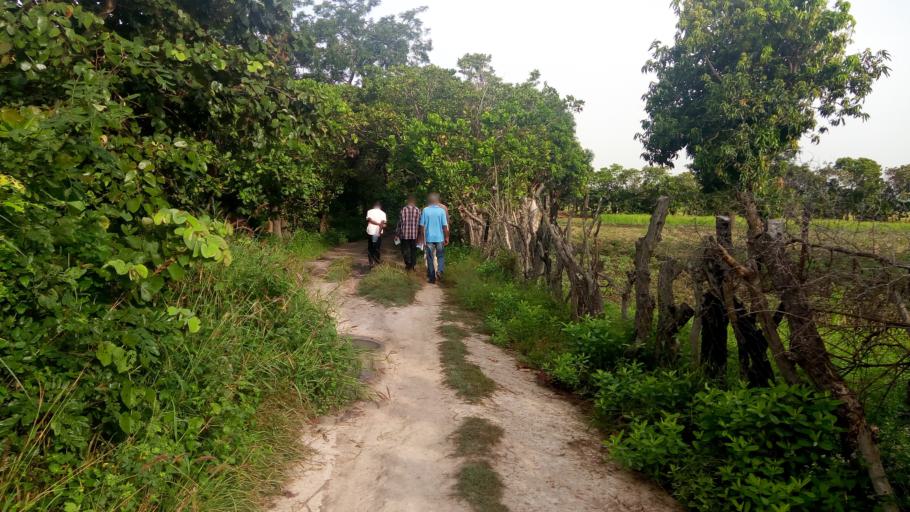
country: ML
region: Koulikoro
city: Kangaba
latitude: 11.6571
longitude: -8.7263
